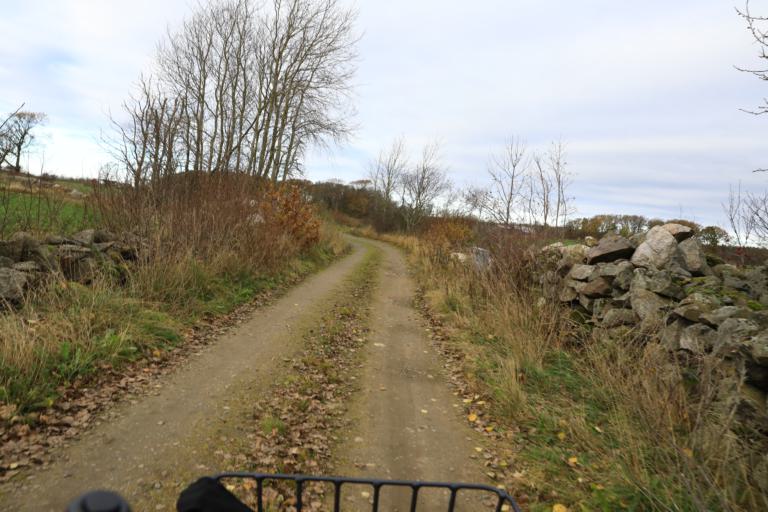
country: SE
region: Halland
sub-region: Varbergs Kommun
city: Traslovslage
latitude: 57.0584
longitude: 12.3337
